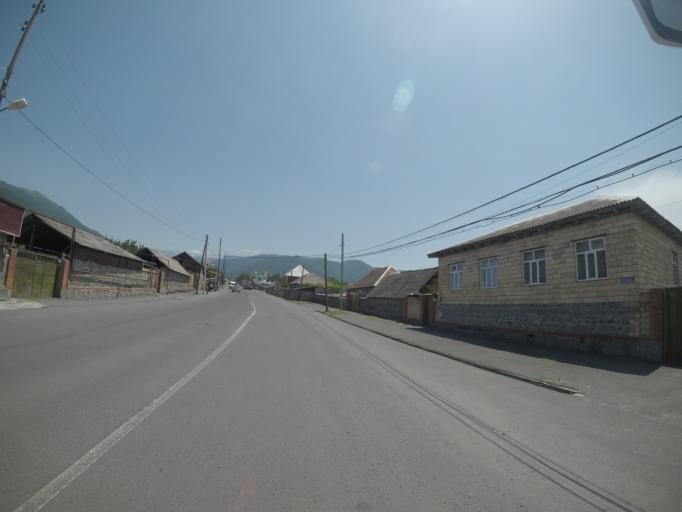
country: AZ
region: Qakh Rayon
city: Qax
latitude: 41.4145
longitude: 46.9126
